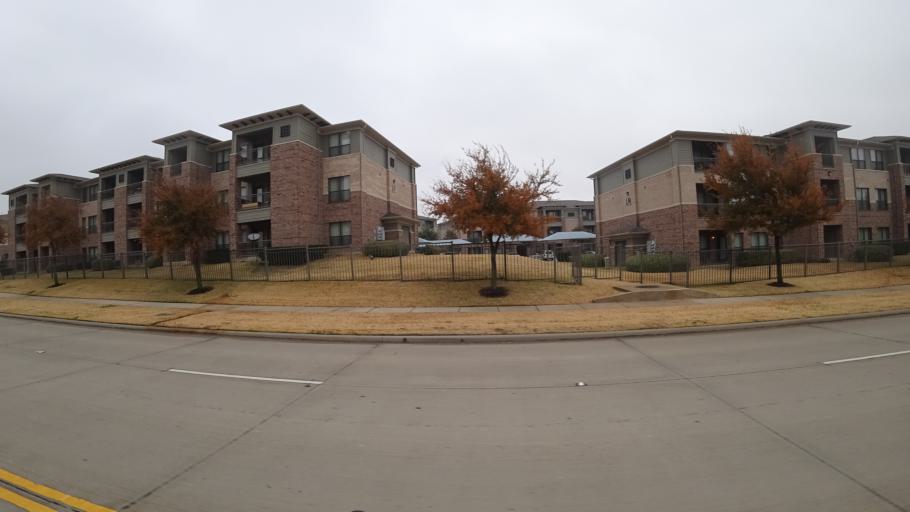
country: US
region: Texas
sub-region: Denton County
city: The Colony
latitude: 33.0608
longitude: -96.9141
